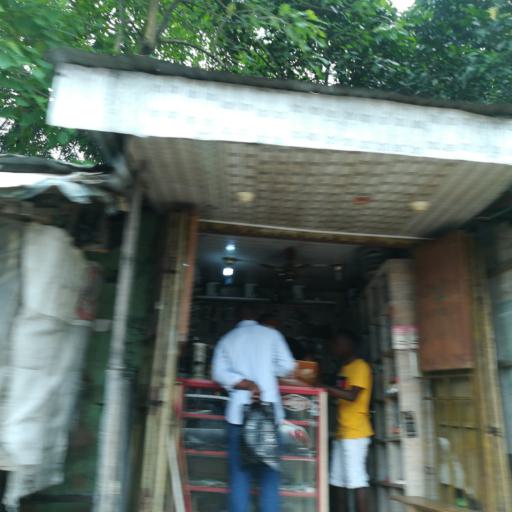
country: NG
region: Rivers
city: Port Harcourt
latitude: 4.8101
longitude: 7.0467
